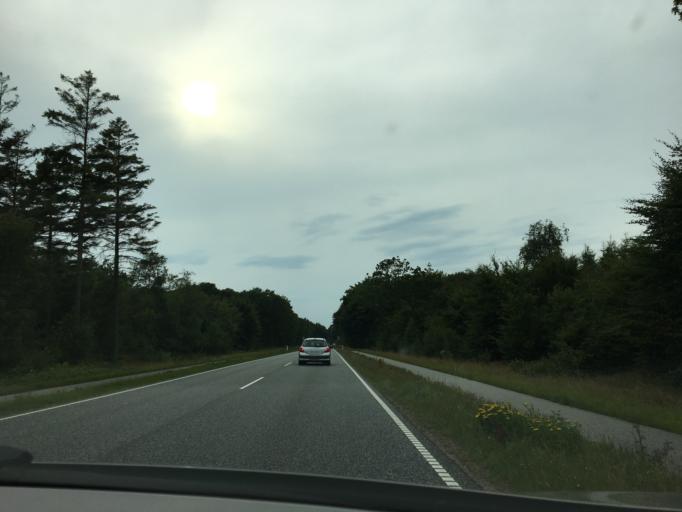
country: DK
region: Central Jutland
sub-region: Ringkobing-Skjern Kommune
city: Ringkobing
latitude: 56.0840
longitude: 8.3244
